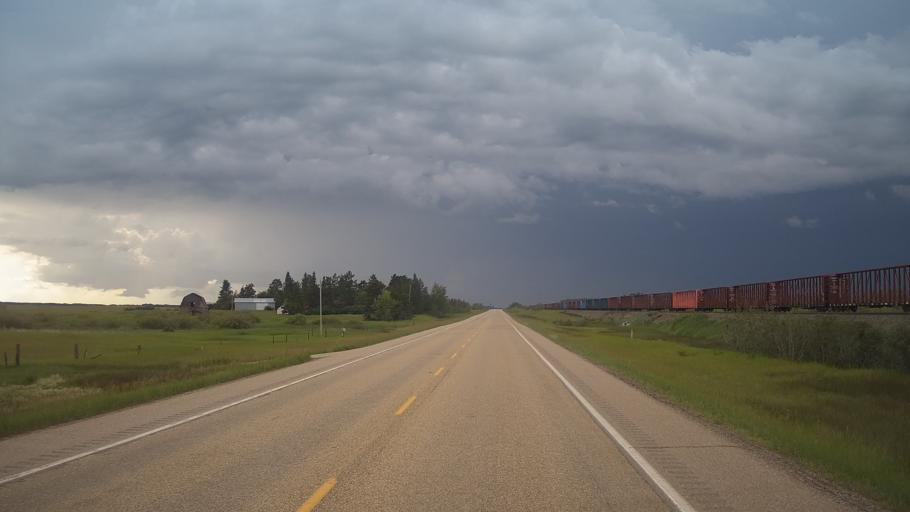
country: CA
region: Alberta
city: Tofield
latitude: 53.2707
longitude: -112.3728
